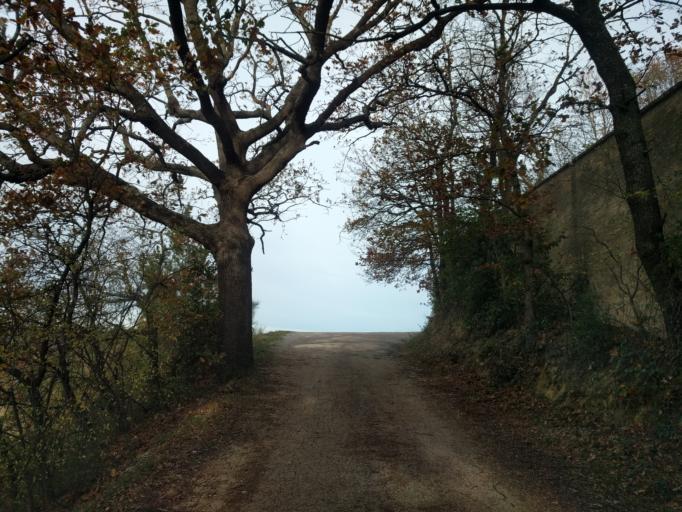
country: IT
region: The Marches
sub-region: Provincia di Pesaro e Urbino
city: Centinarola
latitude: 43.8180
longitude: 12.9723
